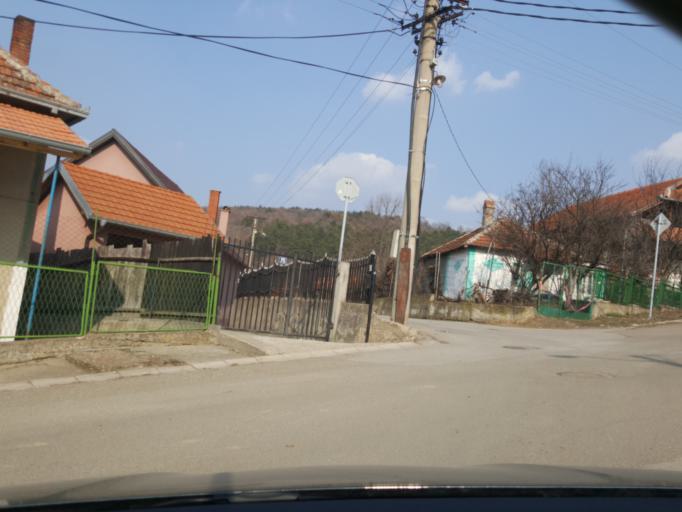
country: RS
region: Central Serbia
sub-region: Nisavski Okrug
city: Aleksinac
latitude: 43.5364
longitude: 21.7179
